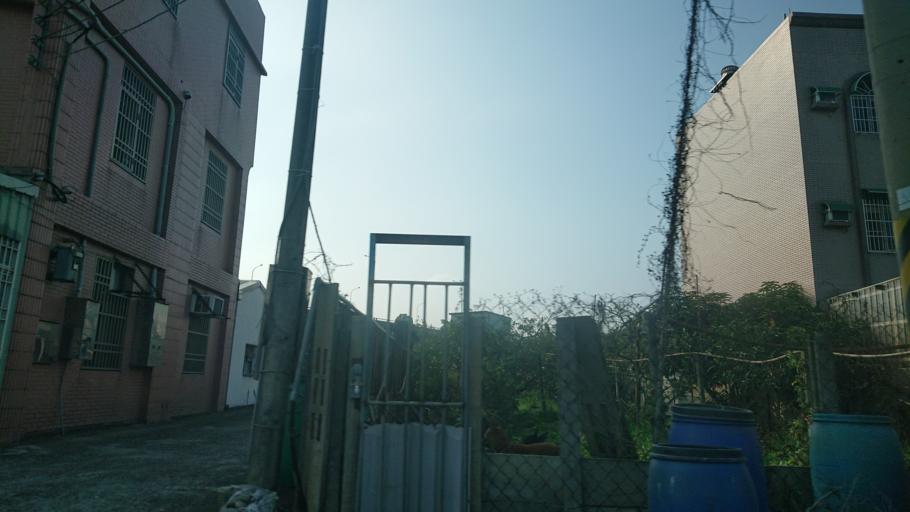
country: TW
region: Taiwan
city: Xinying
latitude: 23.1947
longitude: 120.2714
